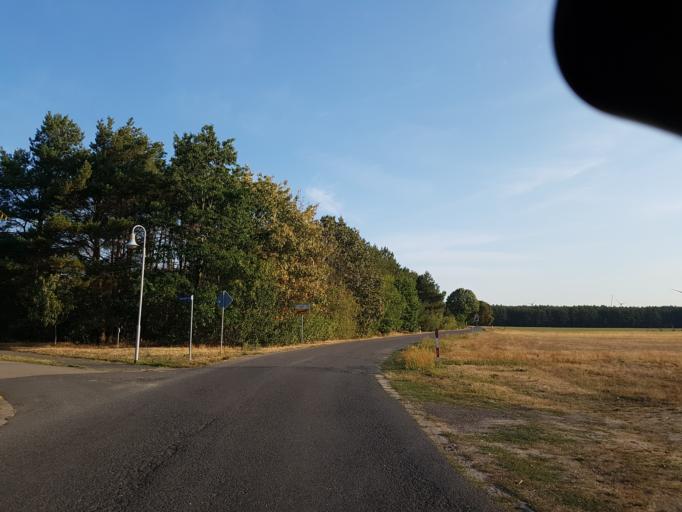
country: DE
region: Saxony-Anhalt
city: Holzdorf
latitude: 51.8319
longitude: 13.1212
